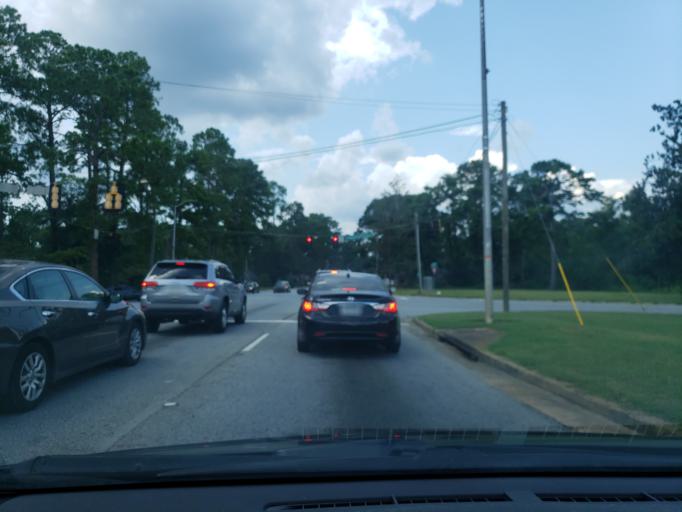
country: US
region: Georgia
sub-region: Dougherty County
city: Albany
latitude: 31.5911
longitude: -84.1911
